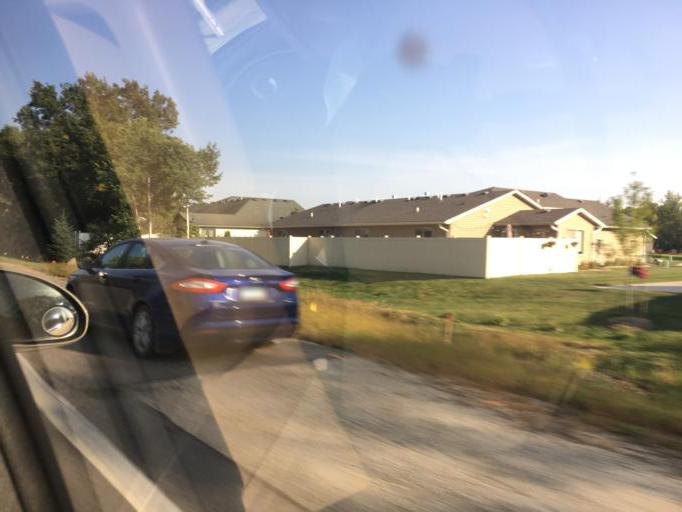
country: US
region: Minnesota
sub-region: Olmsted County
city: Rochester
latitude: 43.9926
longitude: -92.4087
